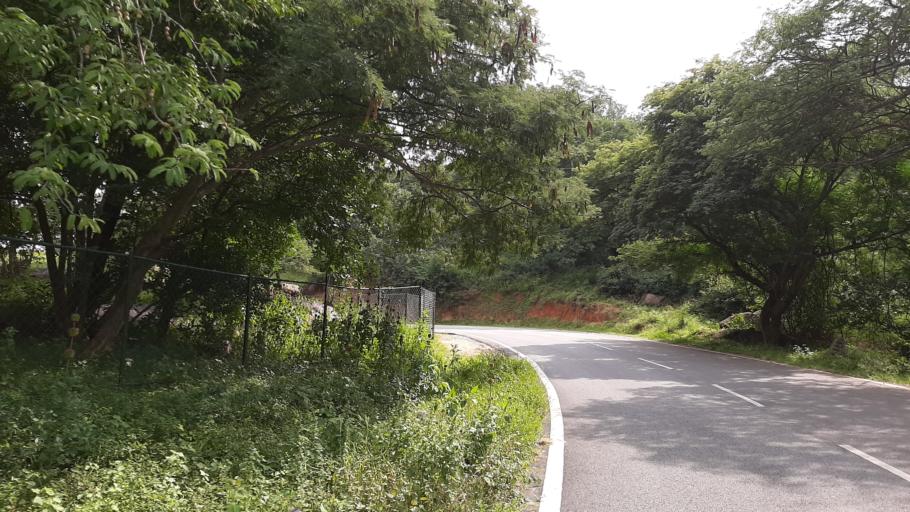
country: IN
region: Karnataka
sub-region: Ramanagara
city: Magadi
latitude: 12.9067
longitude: 77.2938
